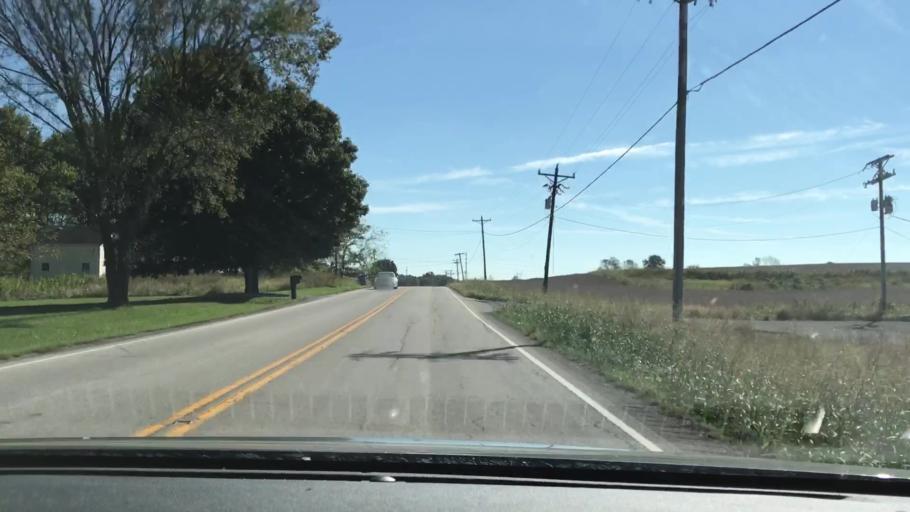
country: US
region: Kentucky
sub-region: Christian County
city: Hopkinsville
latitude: 36.8616
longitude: -87.4386
